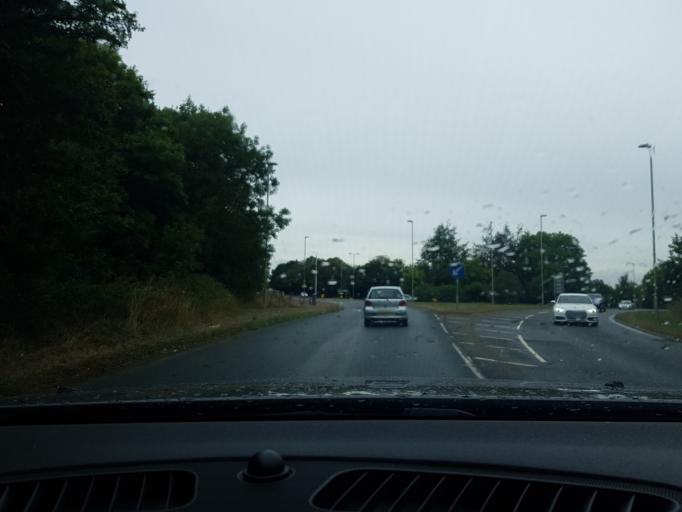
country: GB
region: England
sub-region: Hampshire
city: Odiham
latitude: 51.2560
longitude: -0.9244
